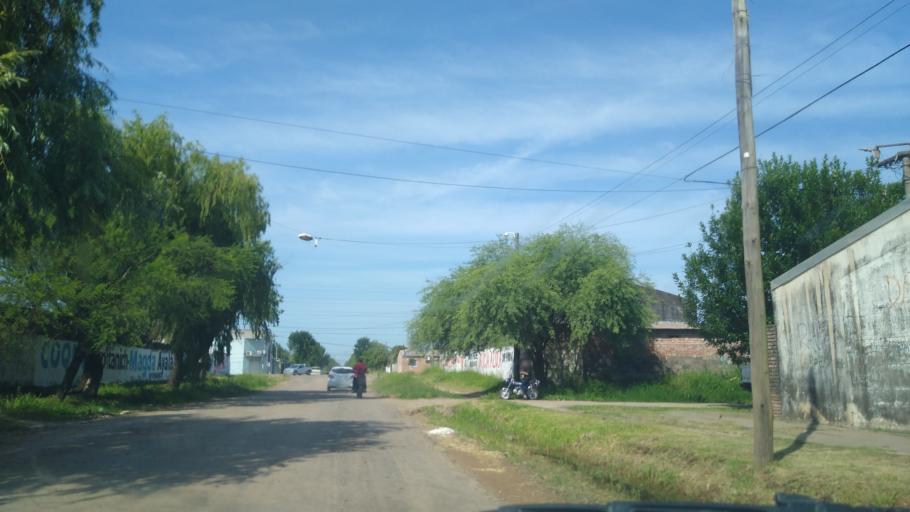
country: AR
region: Chaco
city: Barranqueras
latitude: -27.4940
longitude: -58.9537
